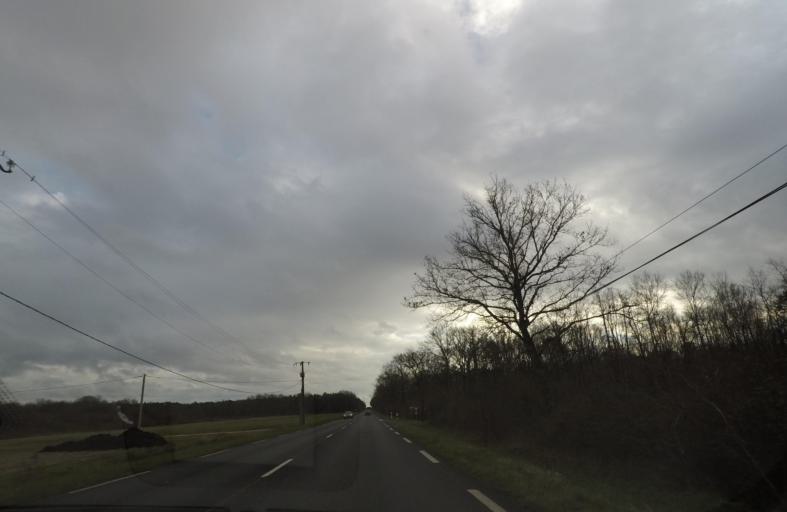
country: FR
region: Centre
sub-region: Departement du Loir-et-Cher
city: Mur-de-Sologne
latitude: 47.4232
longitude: 1.5831
